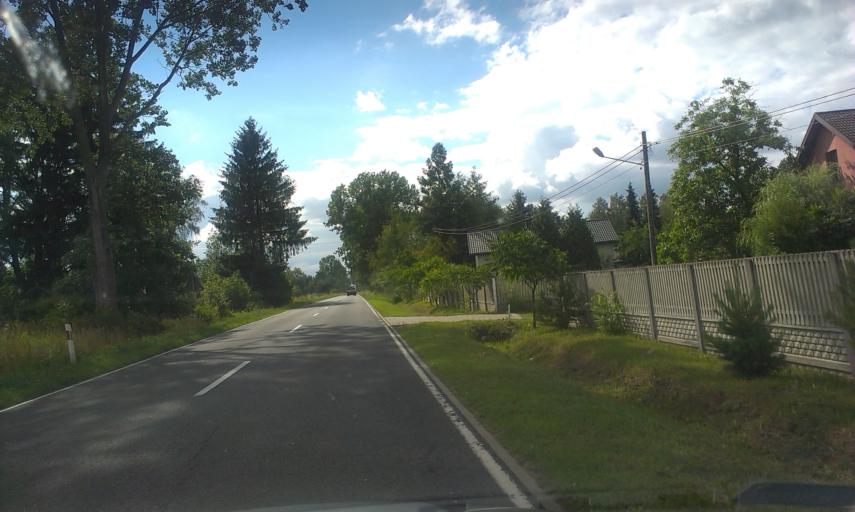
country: PL
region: Lodz Voivodeship
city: Zabia Wola
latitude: 51.9660
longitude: 20.6723
